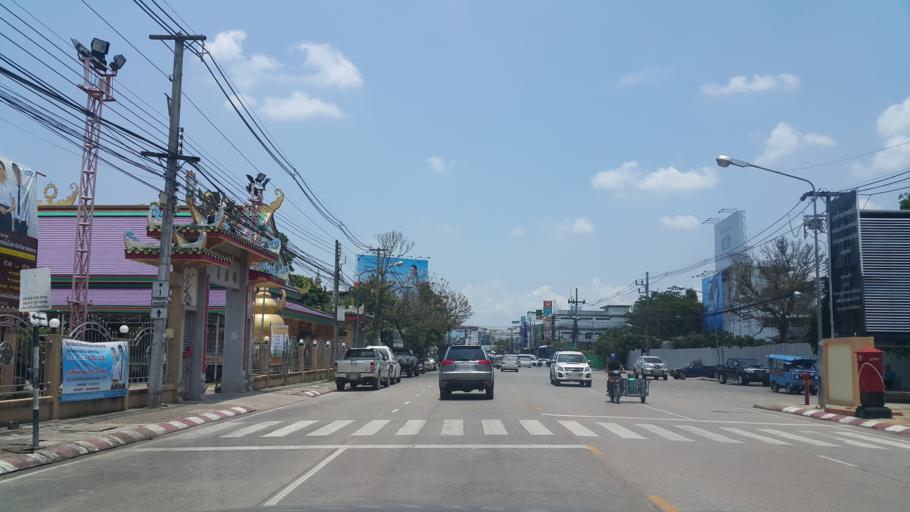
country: TH
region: Chiang Rai
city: Chiang Rai
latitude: 19.9070
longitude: 99.8272
